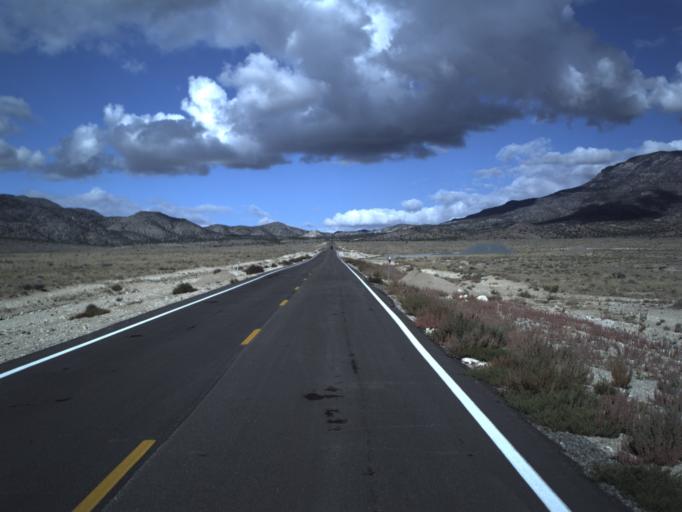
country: US
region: Utah
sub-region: Beaver County
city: Milford
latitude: 38.4922
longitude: -113.4737
